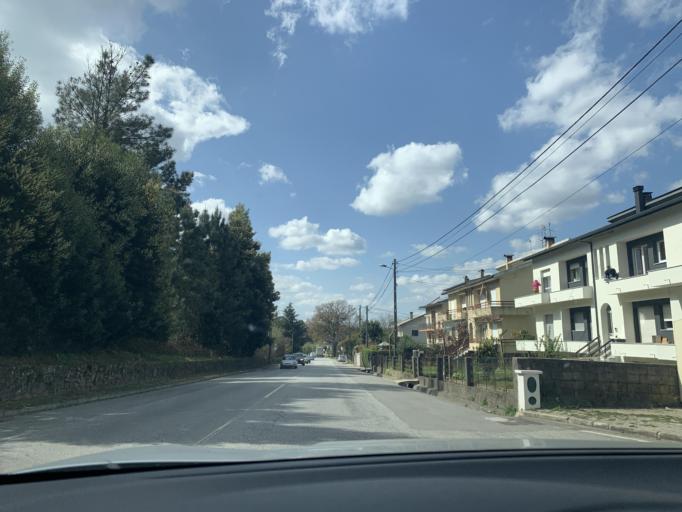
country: PT
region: Viseu
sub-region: Viseu
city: Rio de Loba
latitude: 40.6972
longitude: -7.8713
